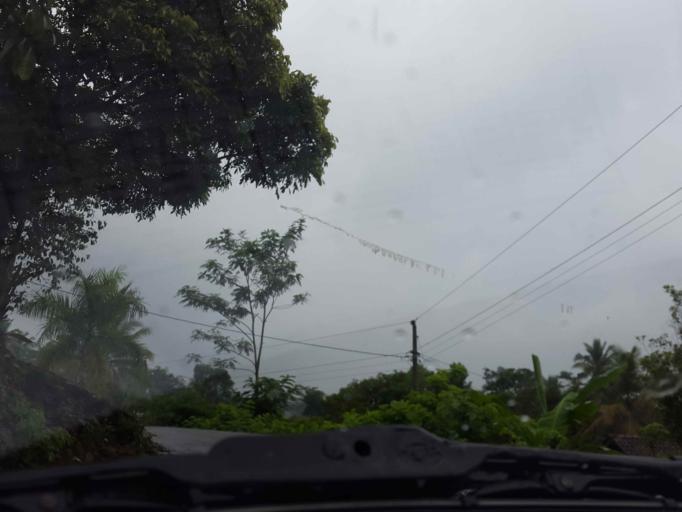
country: ID
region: Central Java
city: Wonosobo
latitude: -7.5204
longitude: 109.8470
